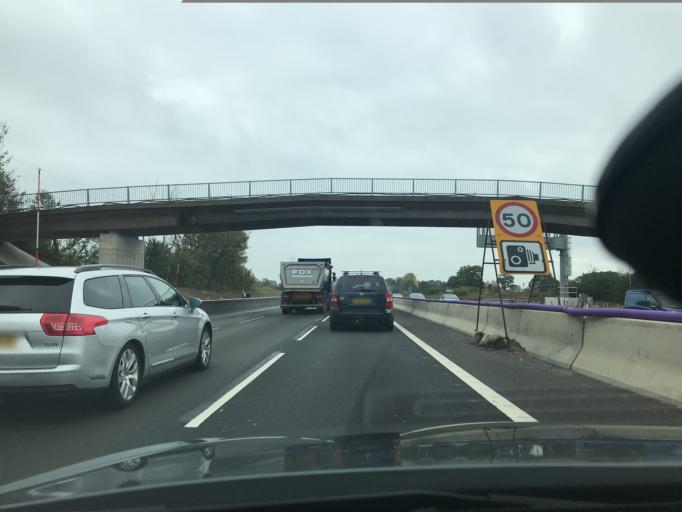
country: GB
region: England
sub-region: Cheshire East
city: Knutsford
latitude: 53.2758
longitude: -2.3976
